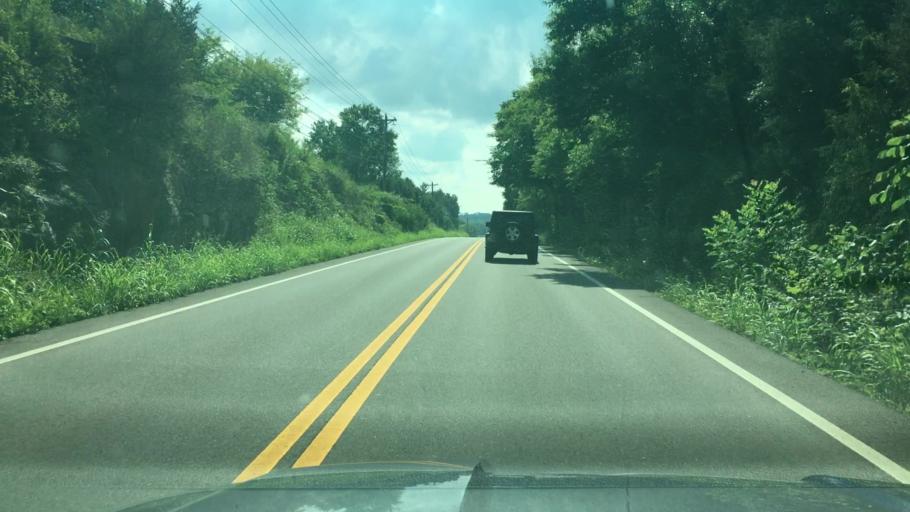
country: US
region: Tennessee
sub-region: Williamson County
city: Nolensville
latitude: 35.8688
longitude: -86.7185
